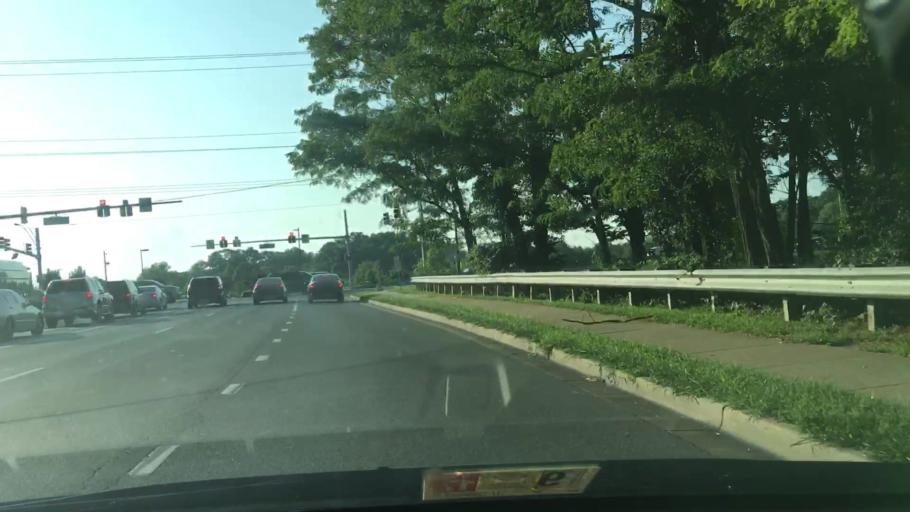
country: US
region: Maryland
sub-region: Montgomery County
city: Derwood
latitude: 39.1208
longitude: -77.1577
